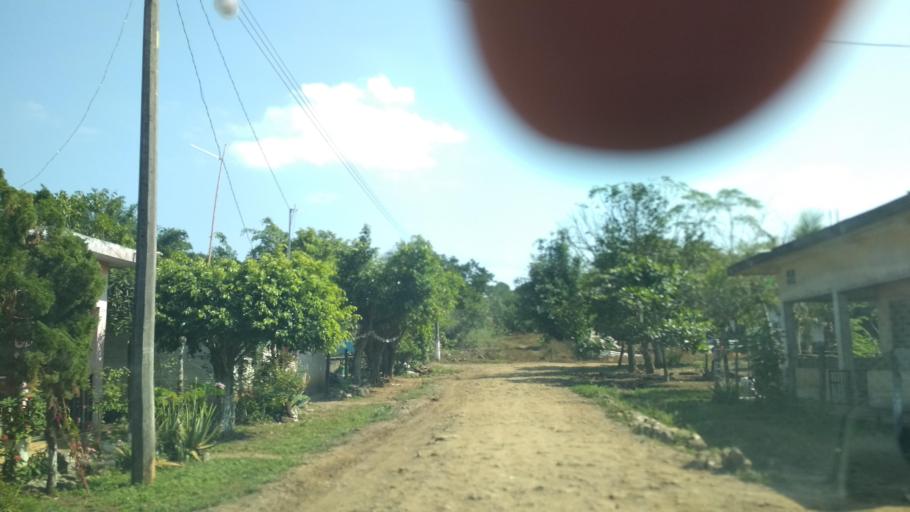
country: MX
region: Puebla
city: San Jose Acateno
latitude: 20.1761
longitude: -97.2287
